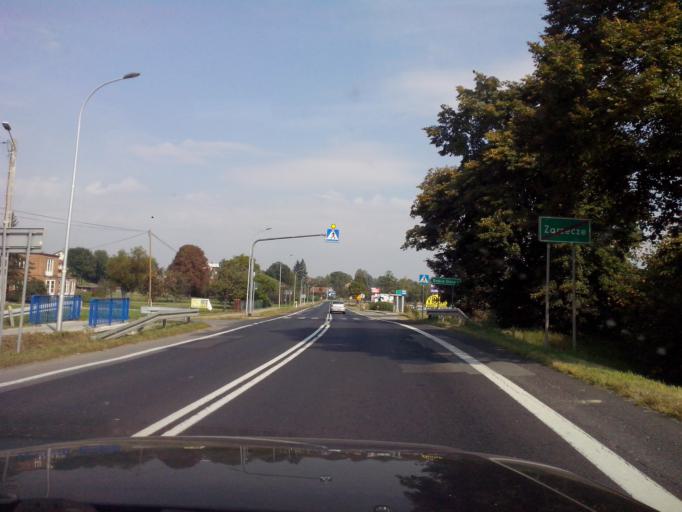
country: PL
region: Subcarpathian Voivodeship
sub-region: Powiat rzeszowski
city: Lutoryz
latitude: 49.9572
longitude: 21.9165
